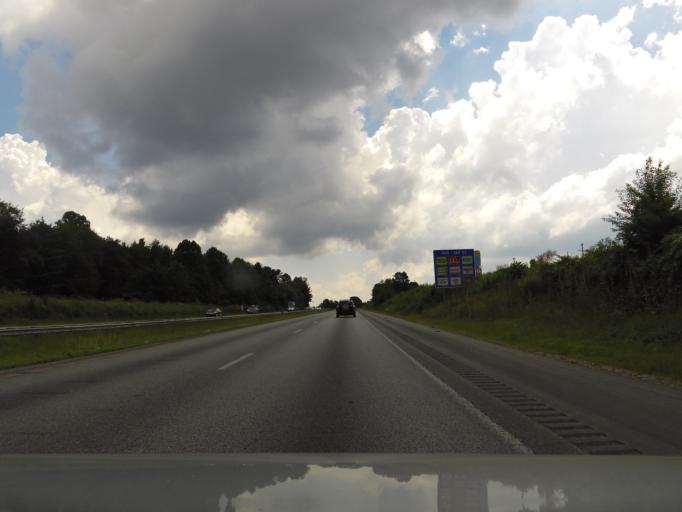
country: US
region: North Carolina
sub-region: Henderson County
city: Barker Heights
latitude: 35.3114
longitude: -82.4180
